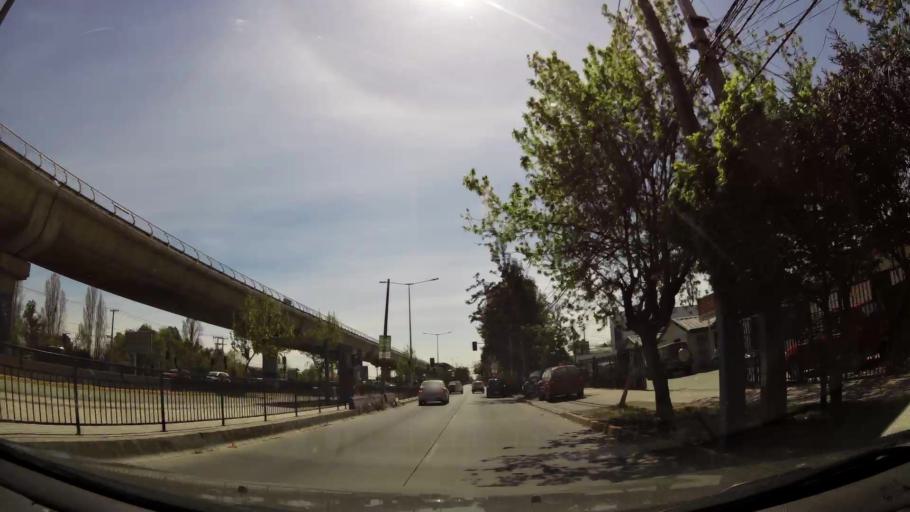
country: CL
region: Santiago Metropolitan
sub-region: Provincia de Cordillera
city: Puente Alto
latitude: -33.5928
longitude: -70.5790
